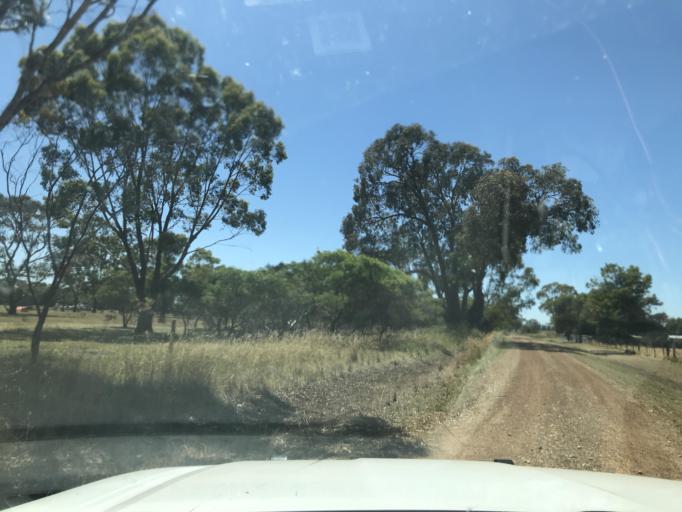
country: AU
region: South Australia
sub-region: Wattle Range
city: Penola
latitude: -37.0553
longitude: 141.2855
